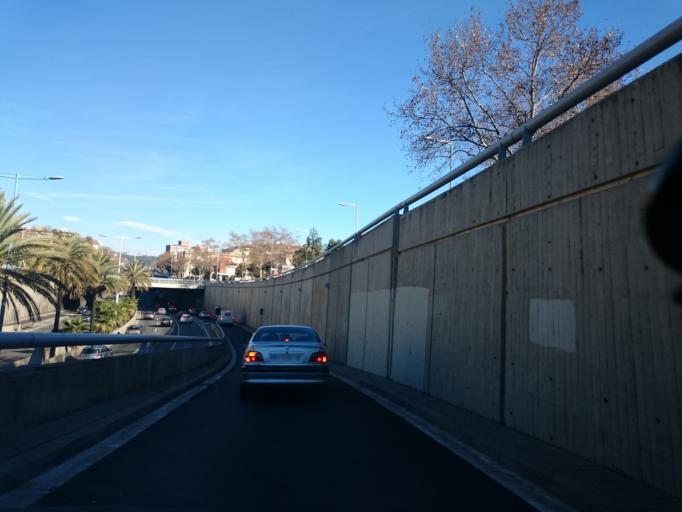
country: ES
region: Catalonia
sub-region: Provincia de Barcelona
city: Sarria-Sant Gervasi
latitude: 41.4163
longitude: 2.1383
